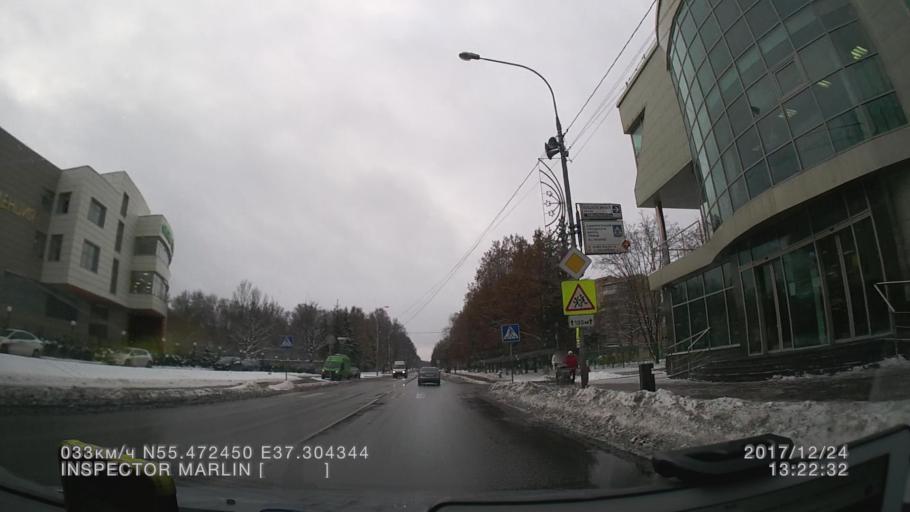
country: RU
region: Moskovskaya
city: Troitsk
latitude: 55.4724
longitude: 37.3043
